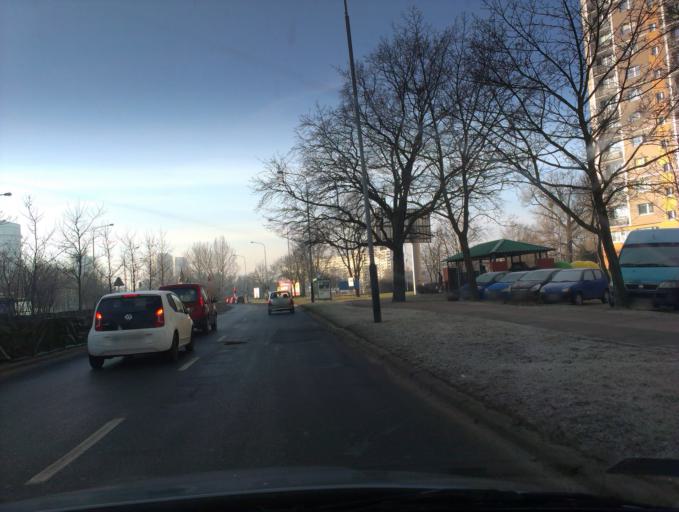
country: PL
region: Greater Poland Voivodeship
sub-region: Poznan
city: Poznan
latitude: 52.3937
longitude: 16.9810
